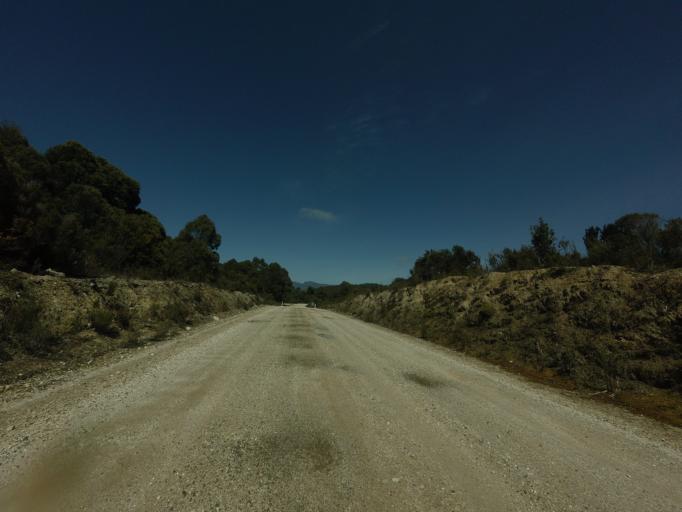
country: AU
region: Tasmania
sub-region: Huon Valley
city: Geeveston
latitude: -43.0280
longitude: 146.3519
